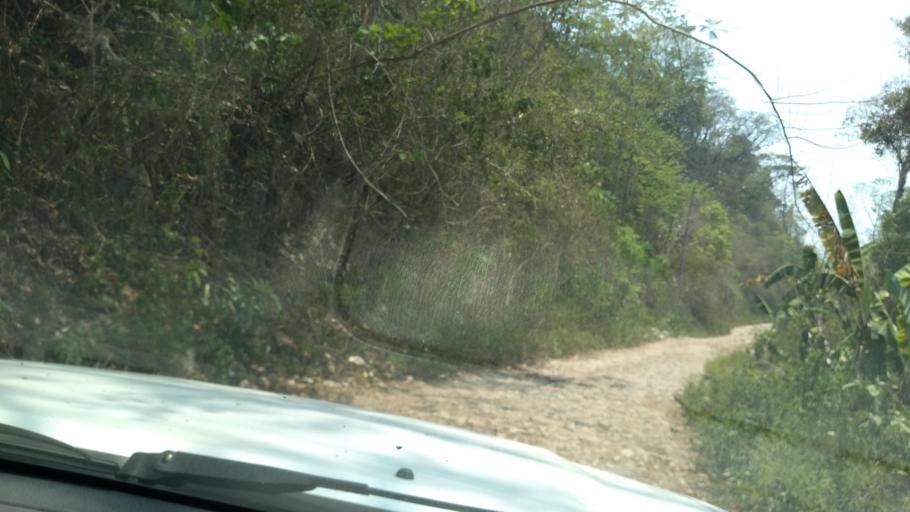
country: MX
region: Veracruz
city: Motzorongo
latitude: 18.5964
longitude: -96.7334
